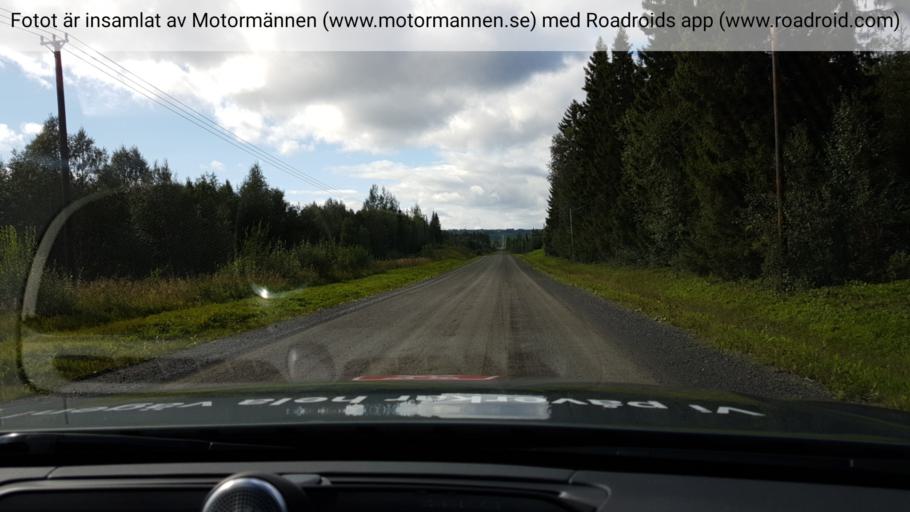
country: SE
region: Jaemtland
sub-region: Stroemsunds Kommun
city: Stroemsund
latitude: 63.6243
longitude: 15.1834
